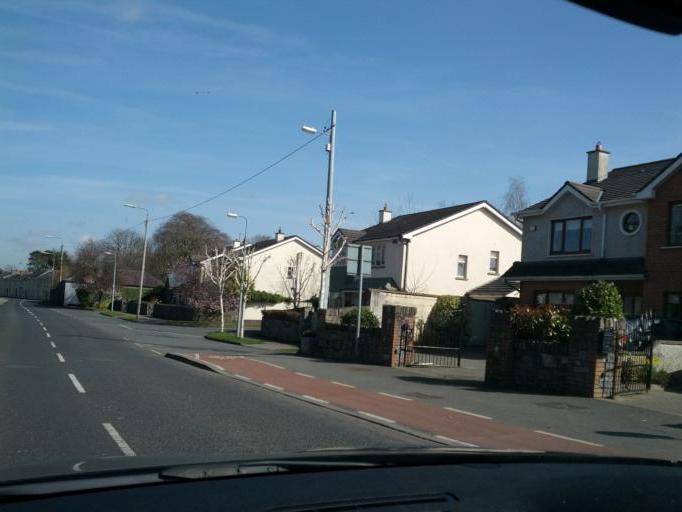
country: IE
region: Leinster
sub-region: Kildare
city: Maynooth
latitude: 53.3778
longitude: -6.5955
